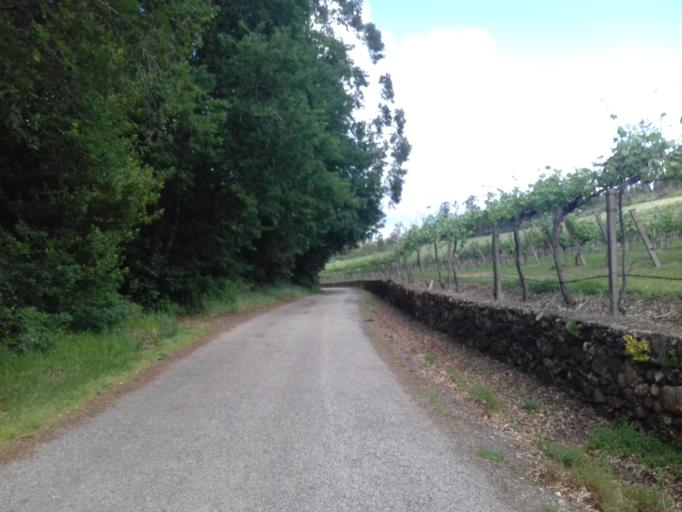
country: ES
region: Galicia
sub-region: Provincia de Pontevedra
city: O Rosal
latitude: 41.9451
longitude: -8.8258
